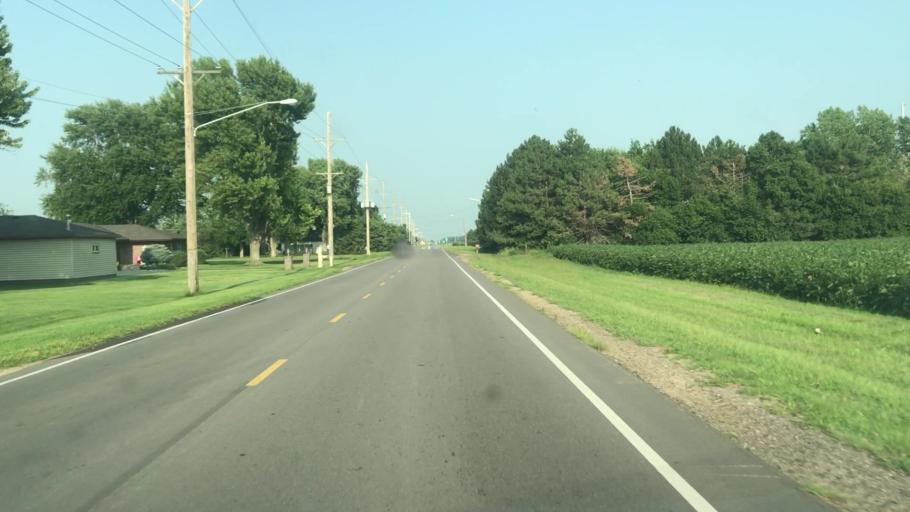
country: US
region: Nebraska
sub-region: Hall County
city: Grand Island
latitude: 40.9455
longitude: -98.3270
